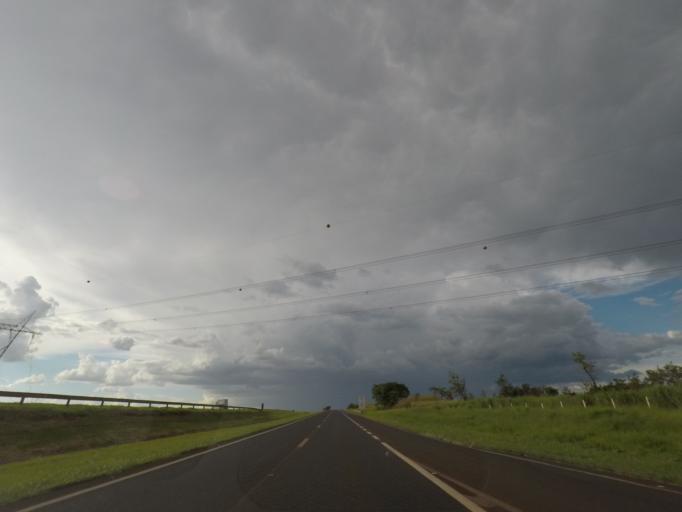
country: BR
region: Sao Paulo
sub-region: Jardinopolis
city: Jardinopolis
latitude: -21.0204
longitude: -47.8402
